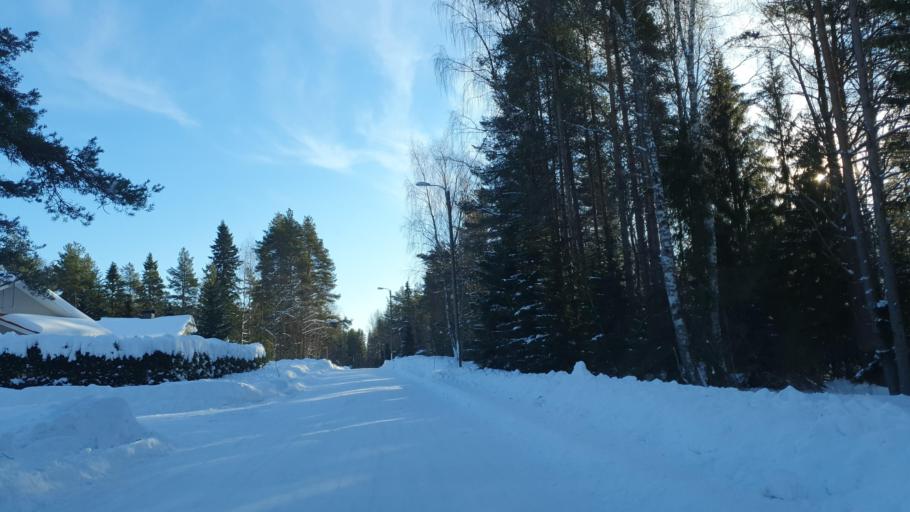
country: FI
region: Northern Ostrobothnia
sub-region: Oulu
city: Haukipudas
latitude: 65.1933
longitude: 25.4145
